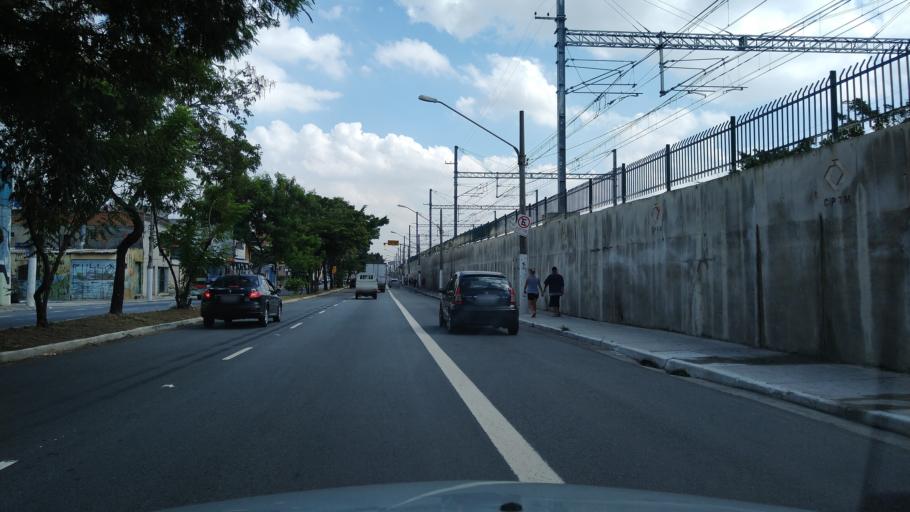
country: BR
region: Sao Paulo
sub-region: Guarulhos
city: Guarulhos
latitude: -23.5016
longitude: -46.5337
